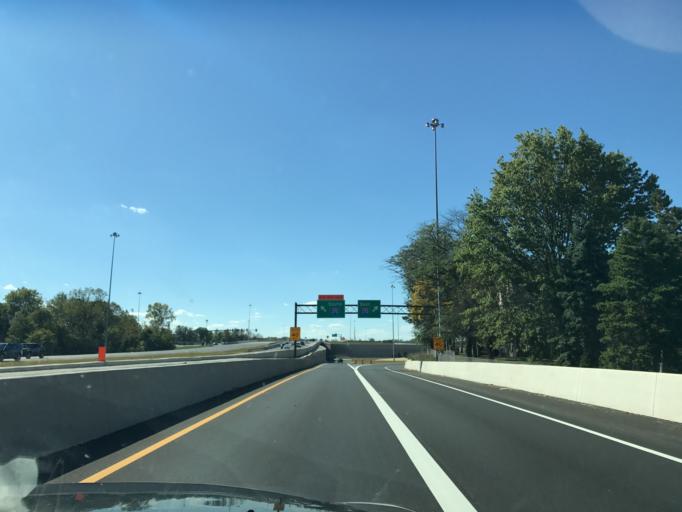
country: US
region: Ohio
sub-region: Franklin County
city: Dublin
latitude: 40.0993
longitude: -83.1281
